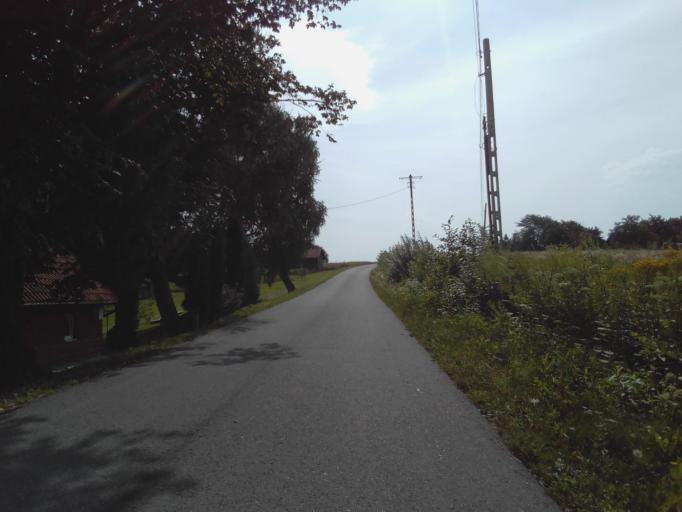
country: PL
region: Subcarpathian Voivodeship
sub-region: Powiat strzyzowski
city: Frysztak
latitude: 49.8680
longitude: 21.5266
